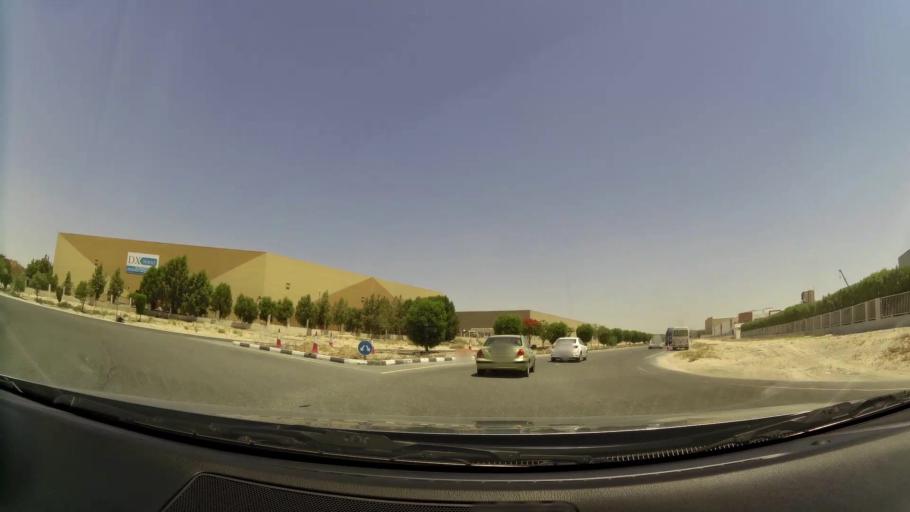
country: AE
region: Dubai
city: Dubai
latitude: 24.9664
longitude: 55.1982
